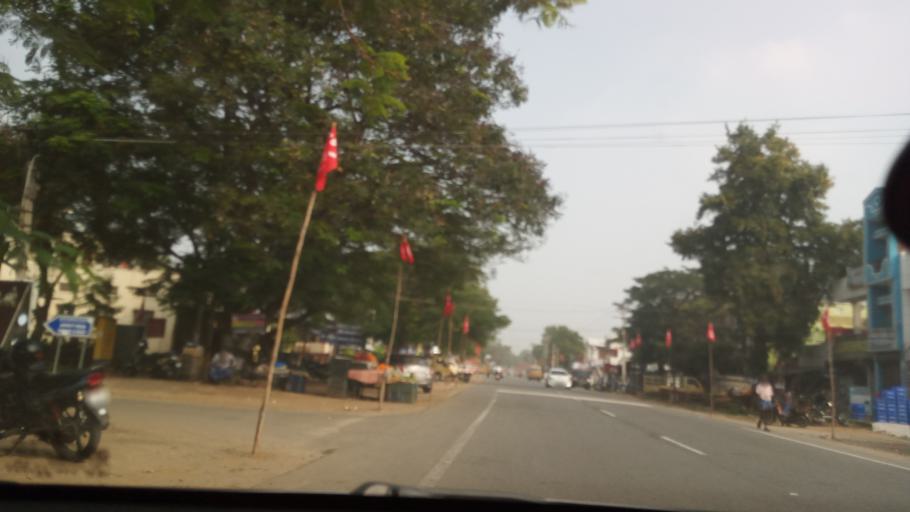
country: IN
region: Tamil Nadu
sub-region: Erode
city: Punjai Puliyampatti
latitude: 11.3549
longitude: 77.1695
